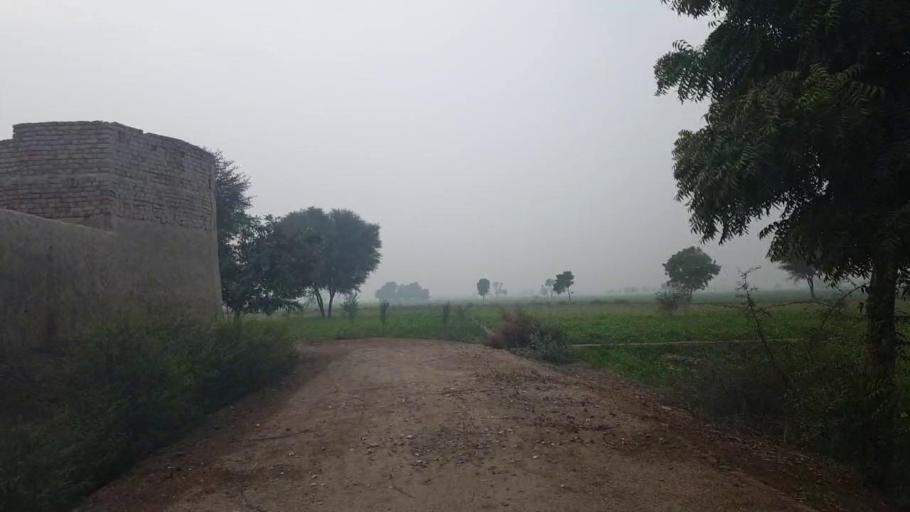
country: PK
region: Sindh
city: Tando Adam
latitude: 25.6889
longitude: 68.6543
